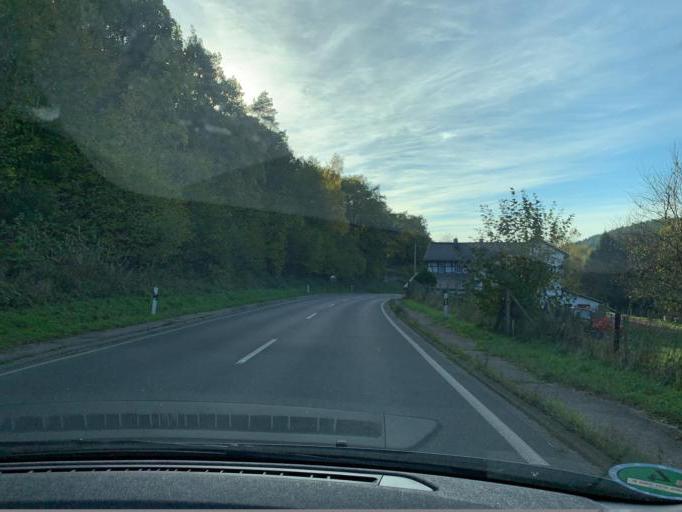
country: DE
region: North Rhine-Westphalia
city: Heimbach
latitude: 50.6362
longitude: 6.5042
